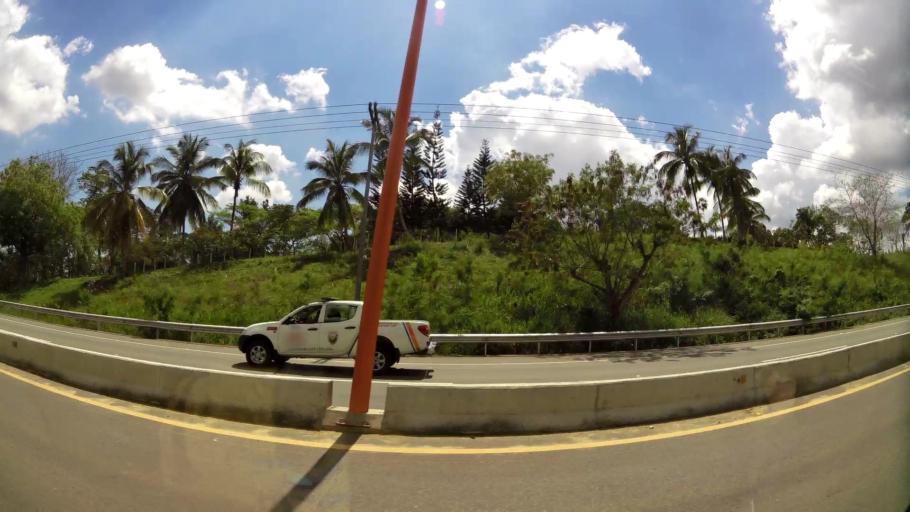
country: DO
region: Nacional
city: Santo Domingo
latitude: 18.5436
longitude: -69.9620
